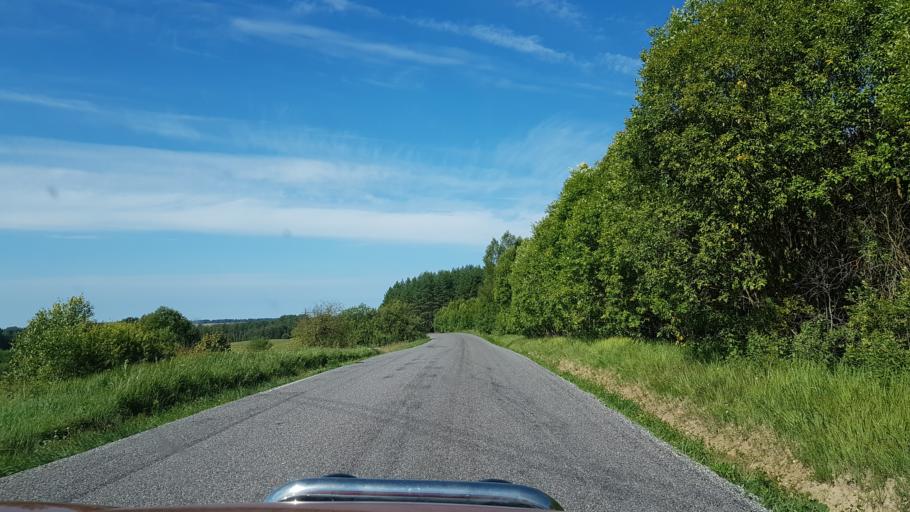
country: EE
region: Tartu
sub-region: Elva linn
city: Elva
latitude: 58.2441
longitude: 26.3948
